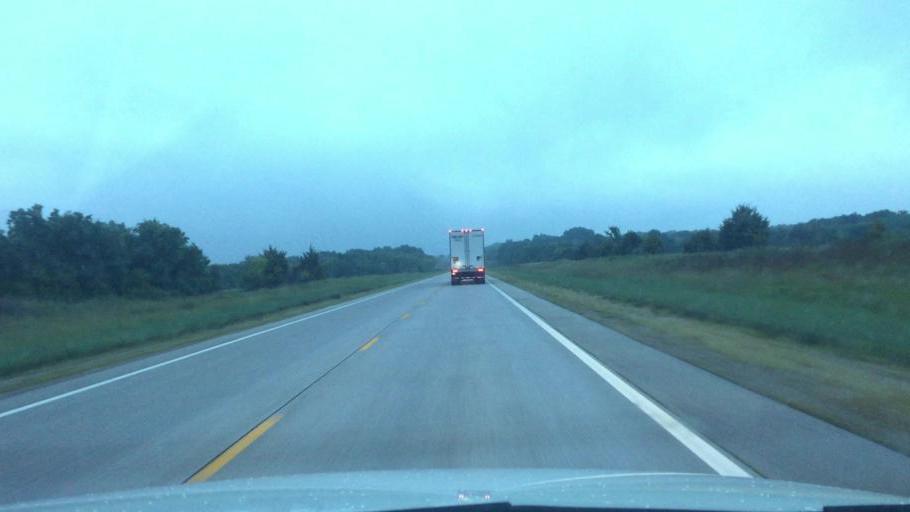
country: US
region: Kansas
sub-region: Neosho County
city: Chanute
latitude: 37.6277
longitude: -95.4796
